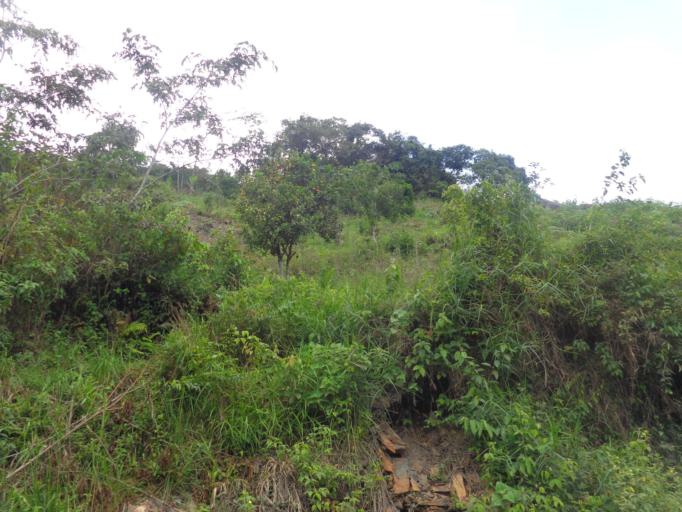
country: BO
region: La Paz
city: Coroico
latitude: -16.1154
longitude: -67.7698
